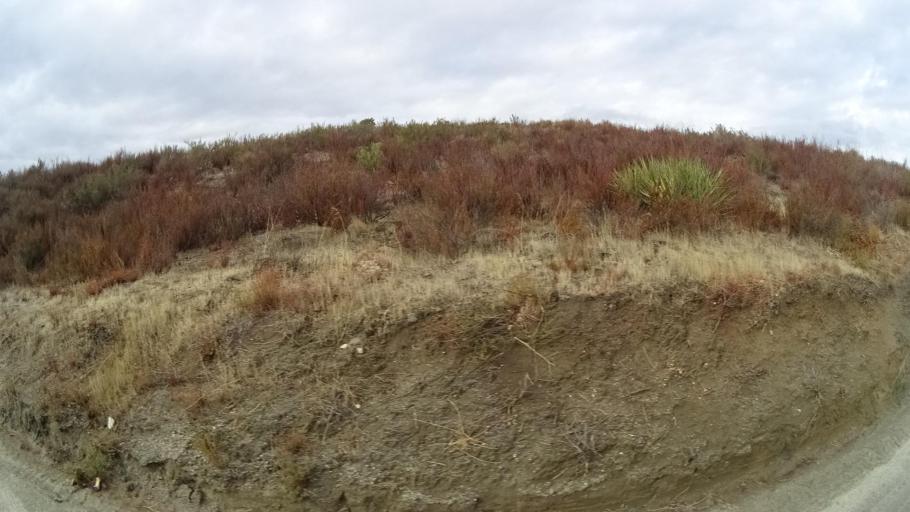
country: MX
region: Baja California
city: Tecate
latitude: 32.5914
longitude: -116.6266
